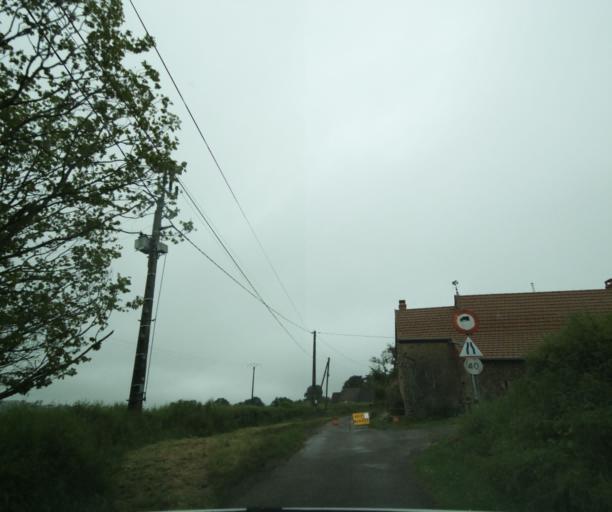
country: FR
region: Bourgogne
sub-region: Departement de Saone-et-Loire
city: Charolles
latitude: 46.3853
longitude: 4.2015
